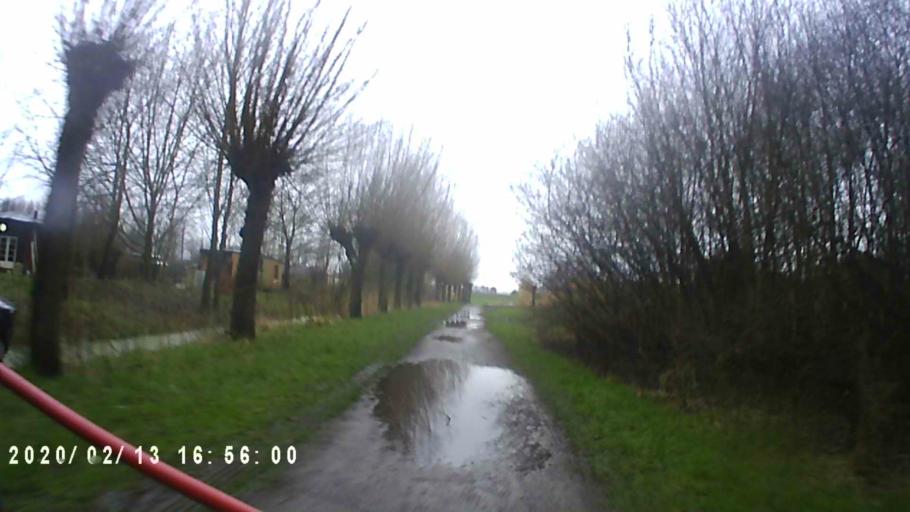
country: NL
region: Groningen
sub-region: Gemeente Groningen
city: Groningen
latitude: 53.2169
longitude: 6.5229
